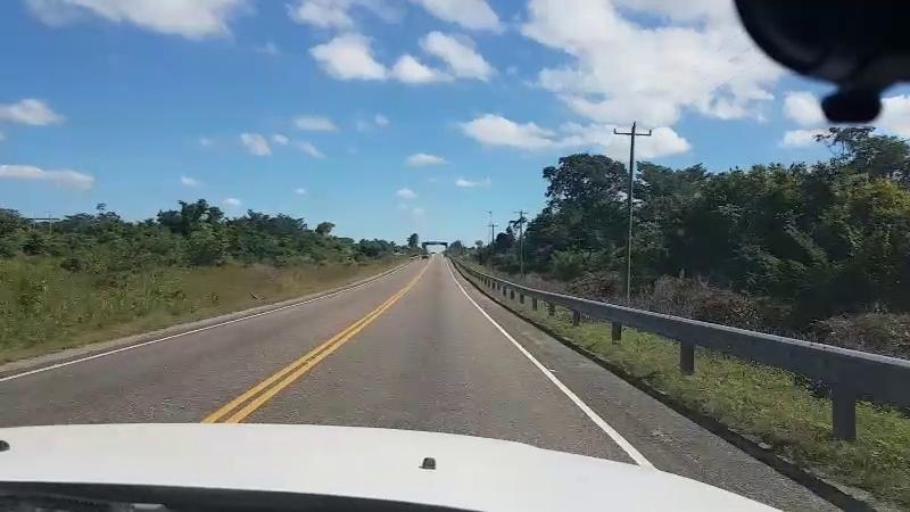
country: BZ
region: Cayo
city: Belmopan
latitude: 17.2771
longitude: -88.6692
